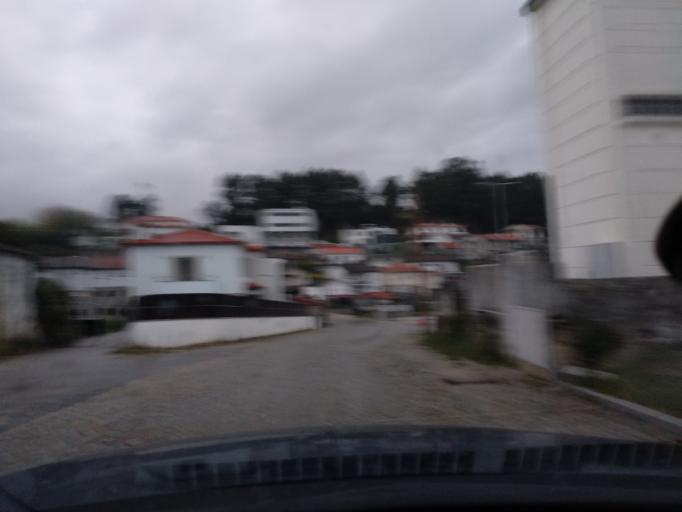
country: PT
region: Porto
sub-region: Penafiel
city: Penafiel
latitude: 41.1910
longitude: -8.2940
